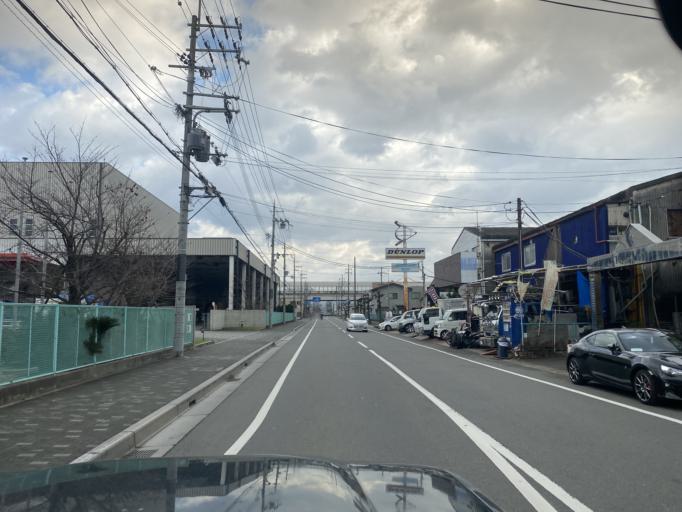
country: JP
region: Kyoto
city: Yawata
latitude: 34.8812
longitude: 135.7462
